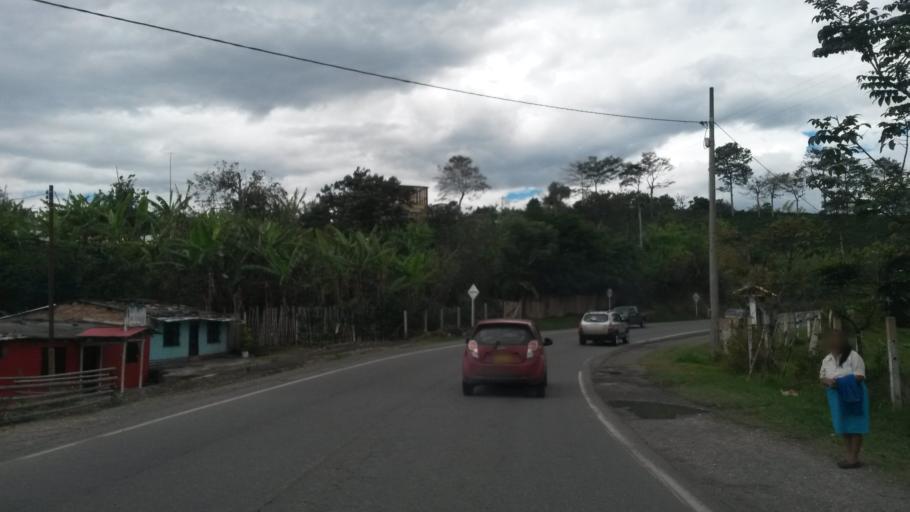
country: CO
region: Cauca
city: Rosas
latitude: 2.3399
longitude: -76.6944
